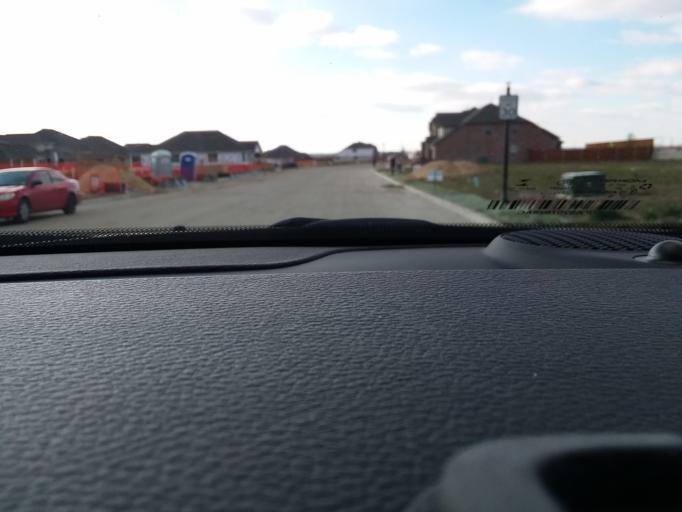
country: US
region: Texas
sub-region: Collin County
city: Prosper
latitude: 33.2650
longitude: -96.8824
